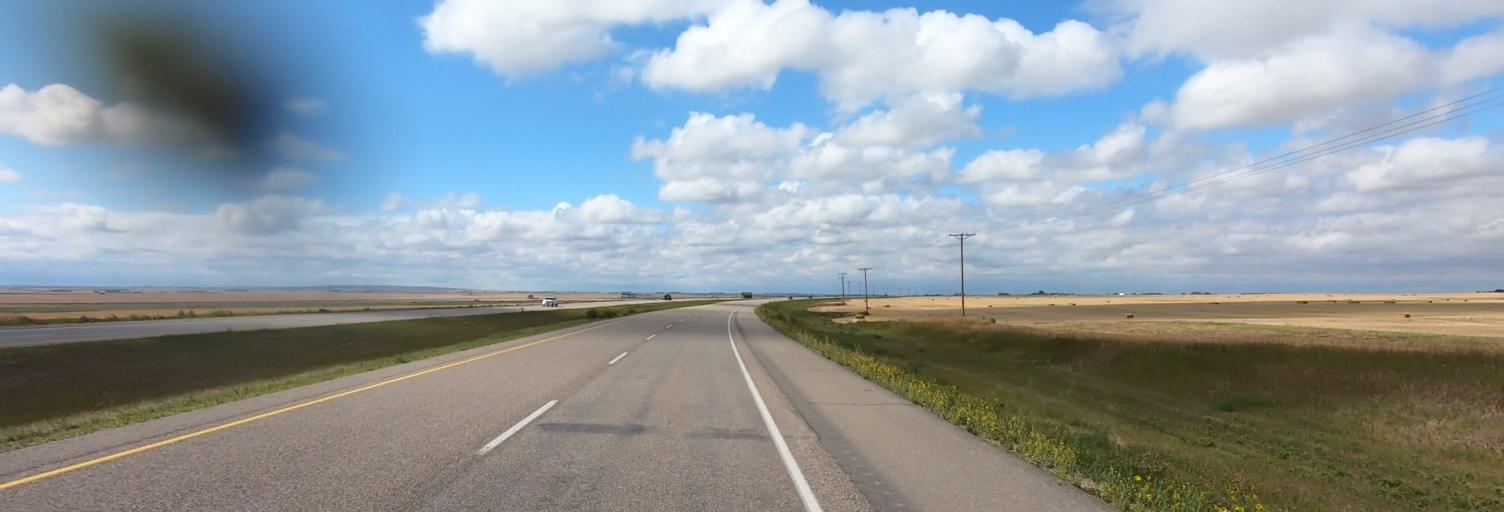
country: CA
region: Saskatchewan
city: Moose Jaw
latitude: 50.4260
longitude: -105.7260
